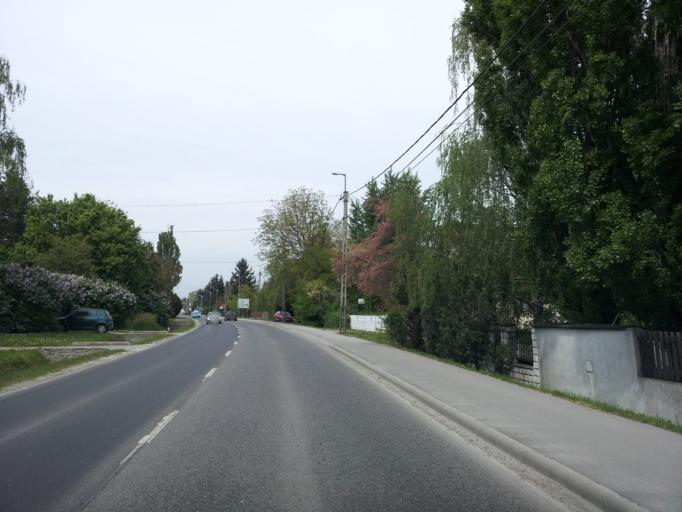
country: HU
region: Pest
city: Tahitotfalu
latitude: 47.7485
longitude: 19.0815
